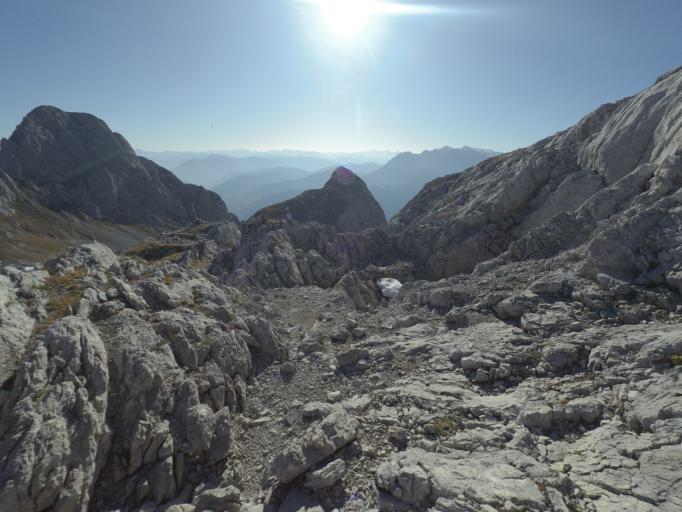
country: AT
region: Salzburg
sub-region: Politischer Bezirk Sankt Johann im Pongau
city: Werfenweng
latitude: 47.4983
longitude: 13.2420
